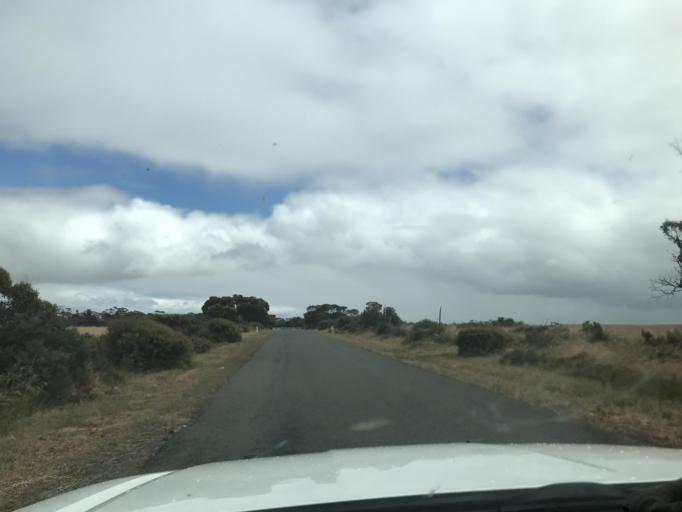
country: AU
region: South Australia
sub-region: Tatiara
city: Bordertown
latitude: -36.1420
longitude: 141.2259
